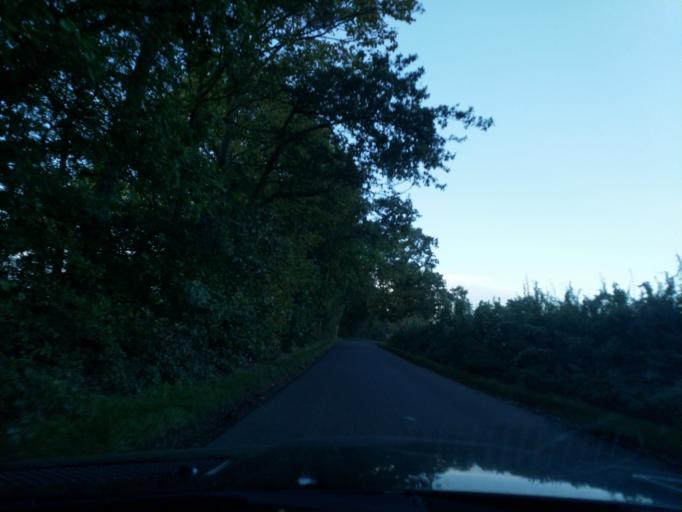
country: GB
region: England
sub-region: Solihull
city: Knowle
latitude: 52.3399
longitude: -1.7460
